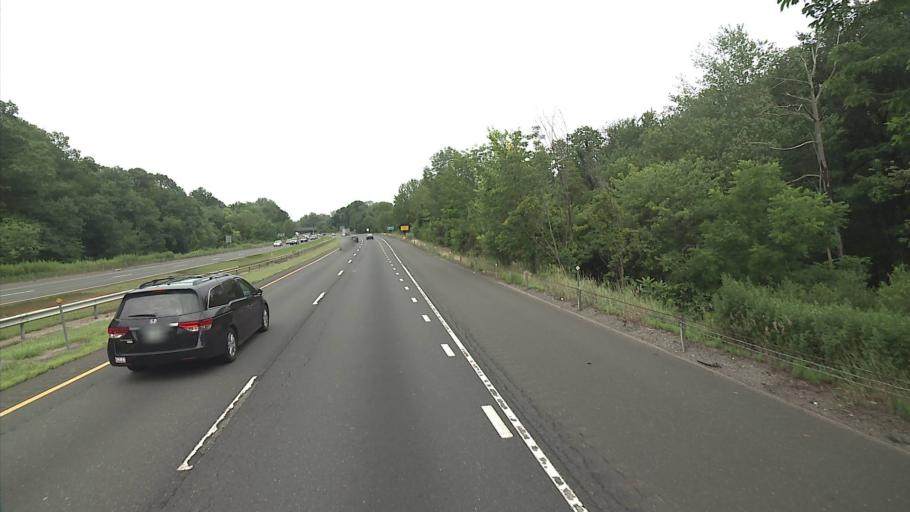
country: US
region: Connecticut
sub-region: Fairfield County
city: Bethel
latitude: 41.4245
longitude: -73.3791
